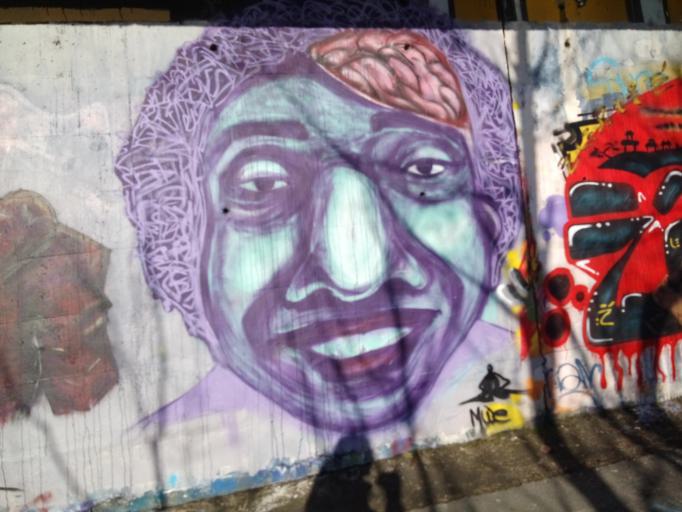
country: FR
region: Rhone-Alpes
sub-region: Departement de l'Isere
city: Saint-Martin-le-Vinoux
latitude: 45.2050
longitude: 5.7109
